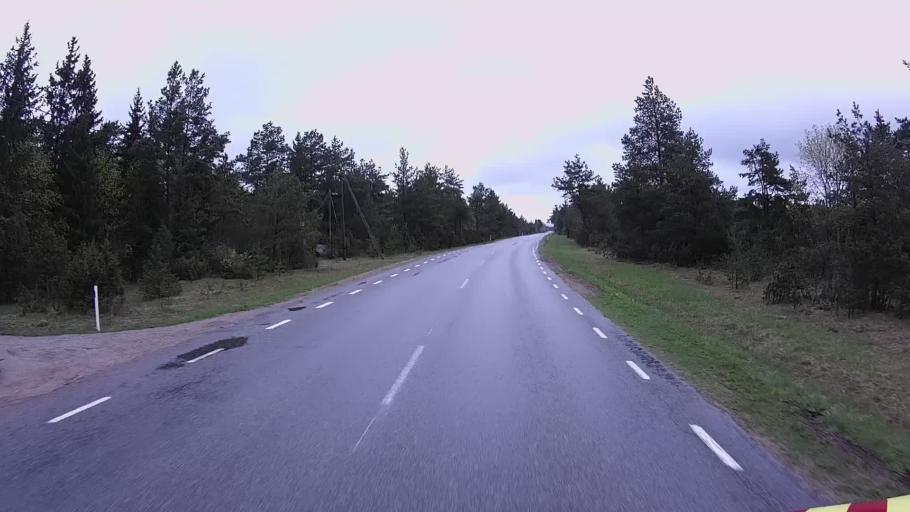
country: EE
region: Saare
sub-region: Kuressaare linn
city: Kuressaare
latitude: 58.3191
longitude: 22.5470
